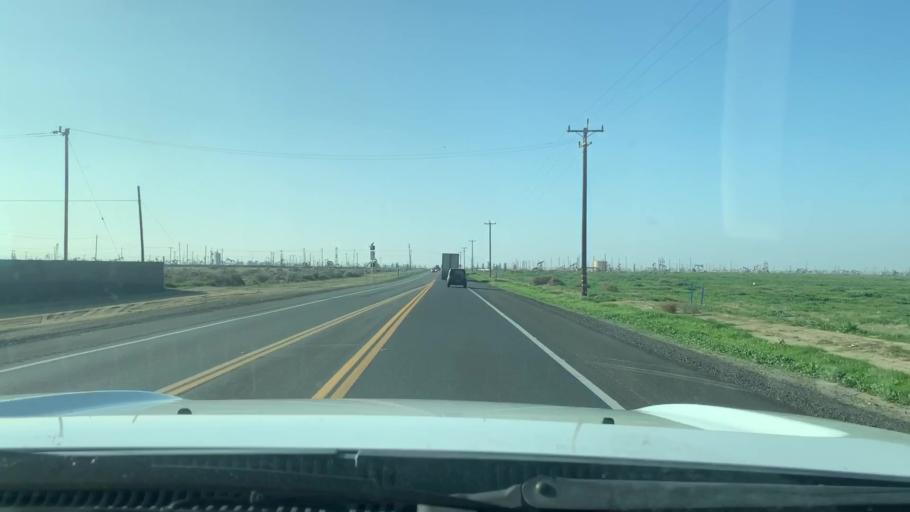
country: US
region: California
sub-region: Kern County
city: Lost Hills
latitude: 35.6160
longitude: -119.7110
